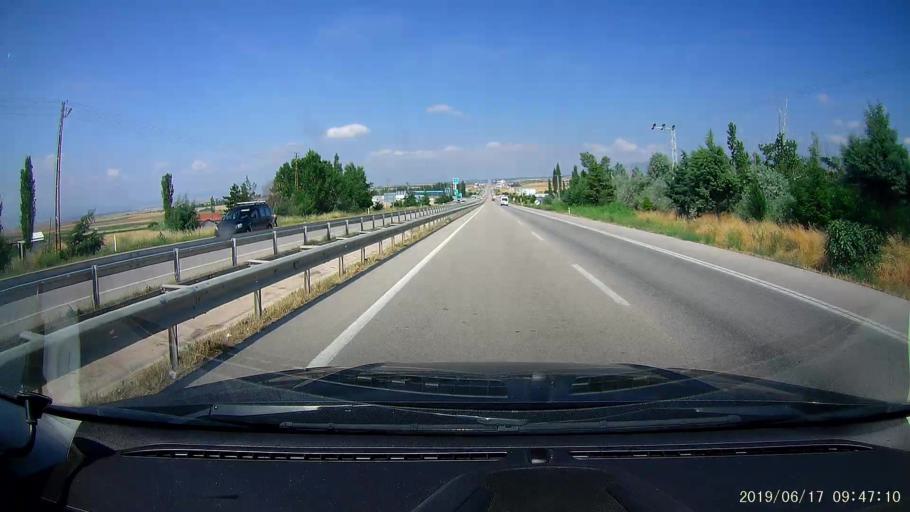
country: TR
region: Amasya
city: Suluova
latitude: 40.8772
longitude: 35.5852
